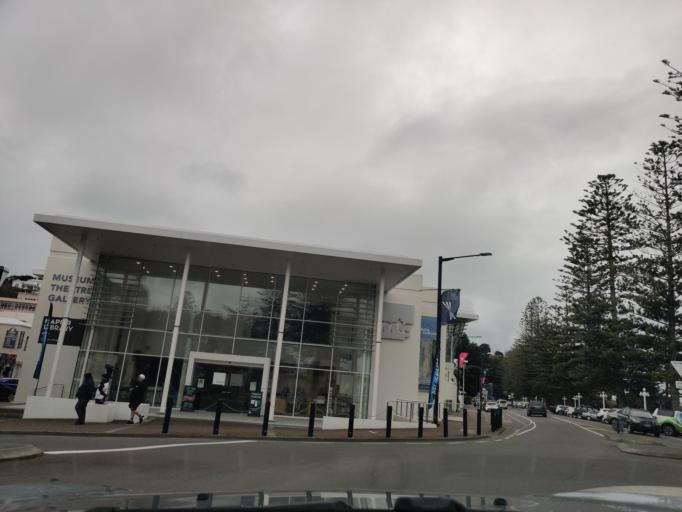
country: NZ
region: Hawke's Bay
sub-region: Napier City
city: Napier
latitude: -39.4893
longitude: 176.9192
